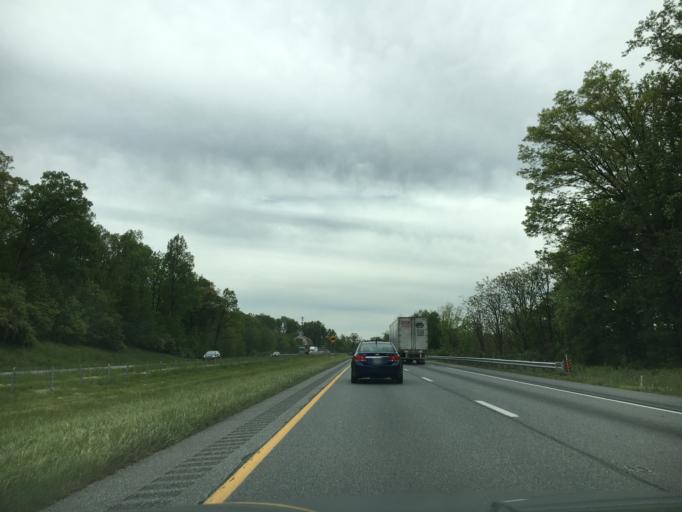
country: US
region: Pennsylvania
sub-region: Lancaster County
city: Reamstown
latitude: 40.1922
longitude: -76.1242
